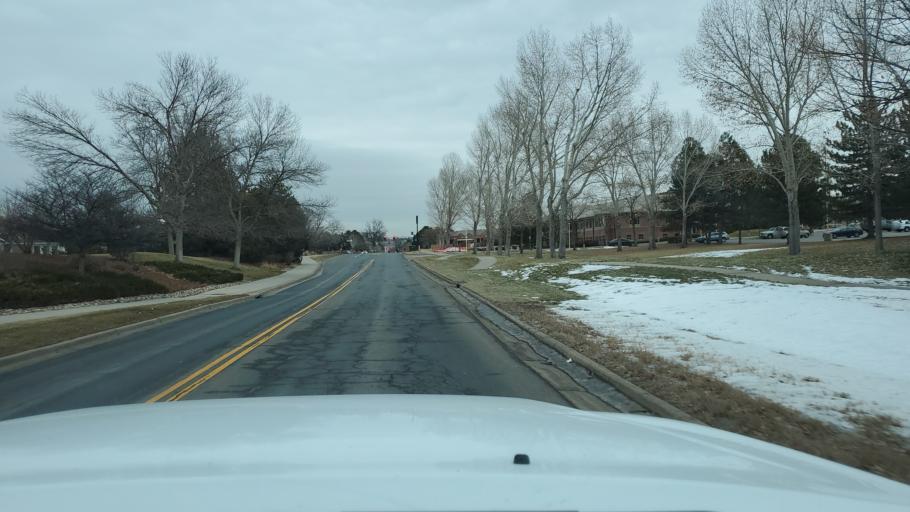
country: US
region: Colorado
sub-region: Arapahoe County
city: Greenwood Village
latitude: 39.6096
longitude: -104.9257
